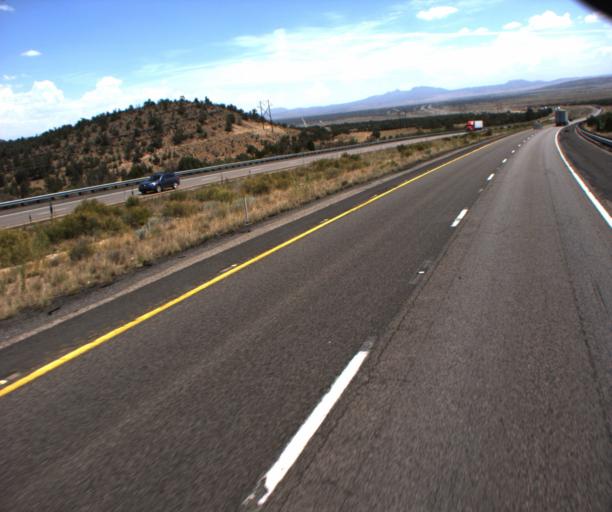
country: US
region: Arizona
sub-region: Mohave County
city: Peach Springs
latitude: 35.3018
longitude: -113.0151
